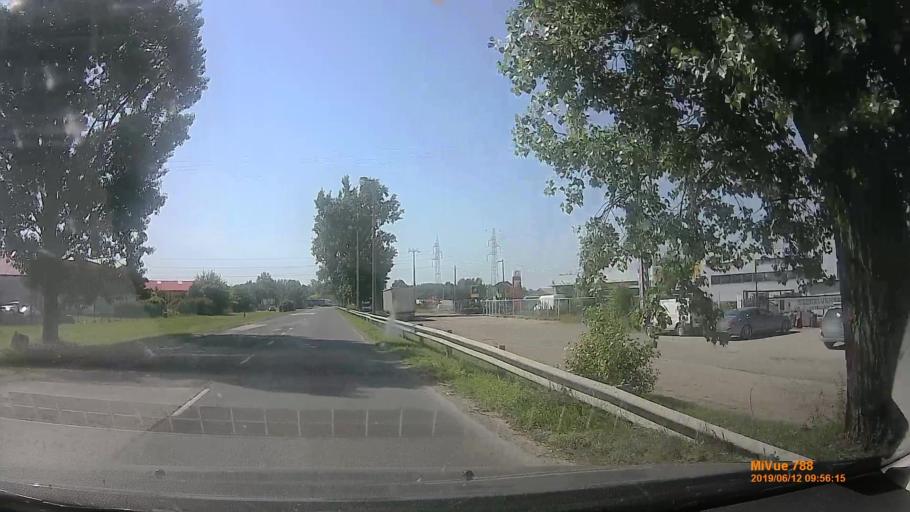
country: HU
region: Pest
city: Alsonemedi
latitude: 47.3057
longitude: 19.1780
